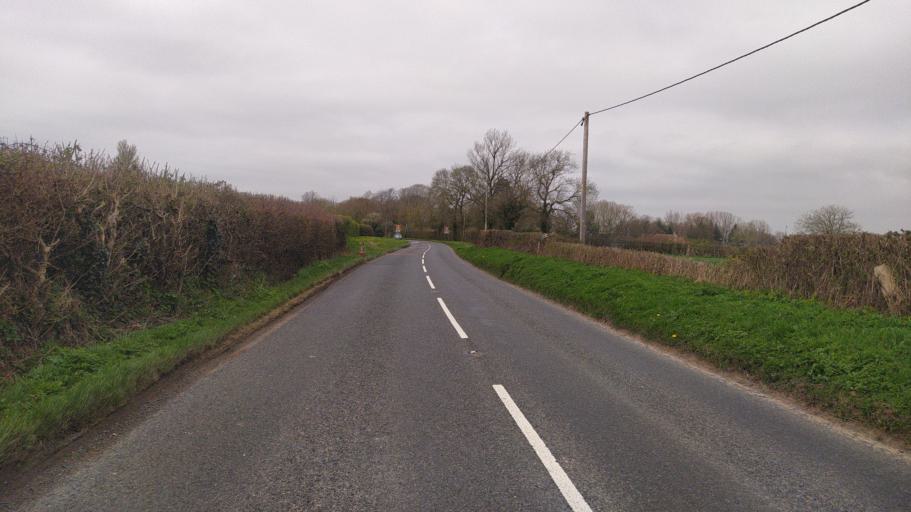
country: GB
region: England
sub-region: Wiltshire
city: Wingfield
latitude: 51.3143
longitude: -2.2489
